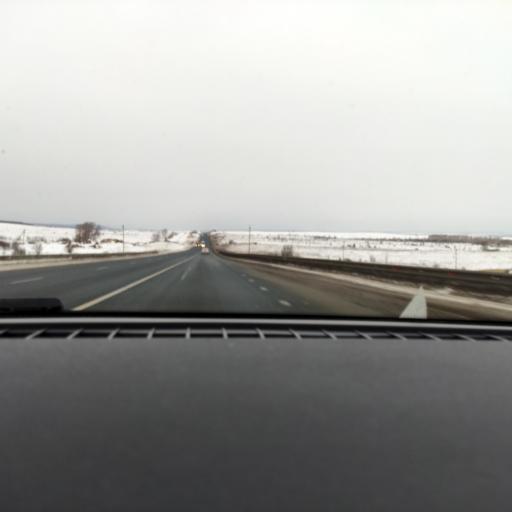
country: RU
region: Samara
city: Novosemeykino
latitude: 53.4003
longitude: 50.4094
